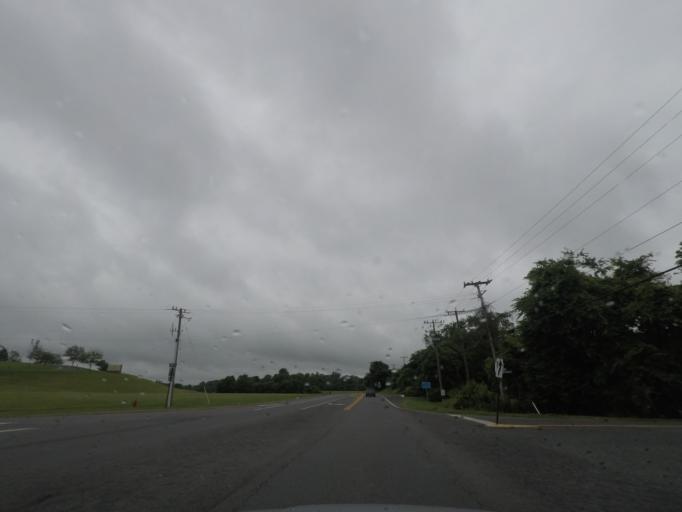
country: US
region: Virginia
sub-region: Orange County
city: Orange
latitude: 38.2608
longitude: -78.1171
